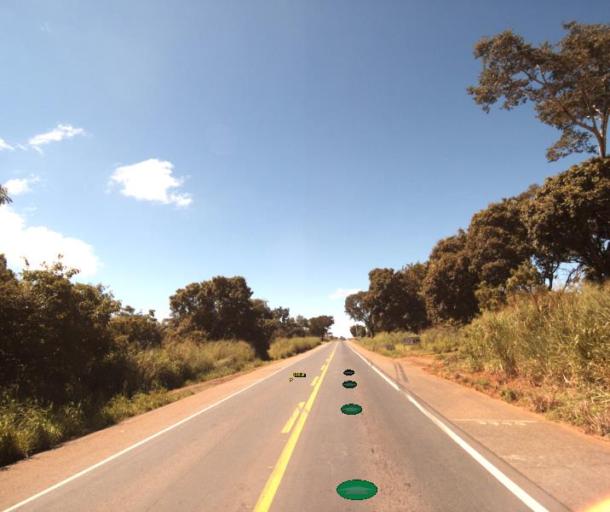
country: BR
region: Goias
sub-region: Jaragua
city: Jaragua
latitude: -15.5589
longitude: -49.4244
